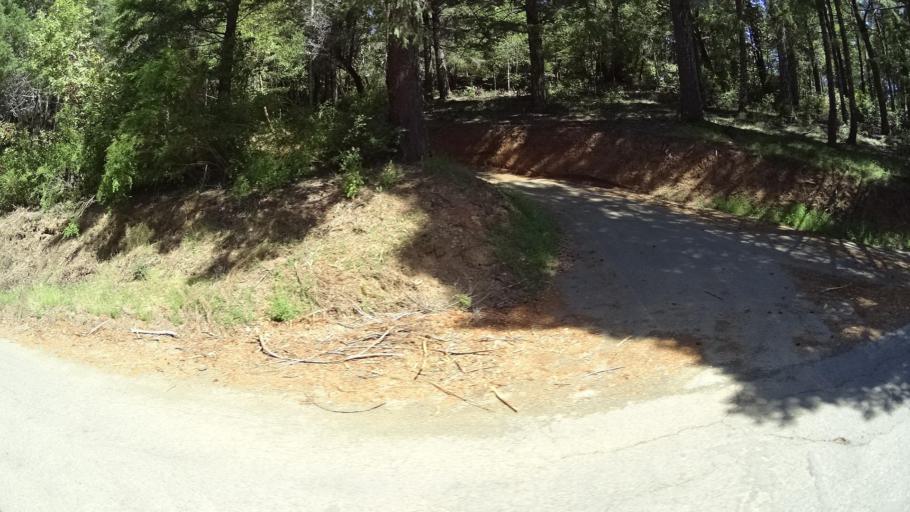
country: US
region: California
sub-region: Humboldt County
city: Redway
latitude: 40.1132
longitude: -123.9626
